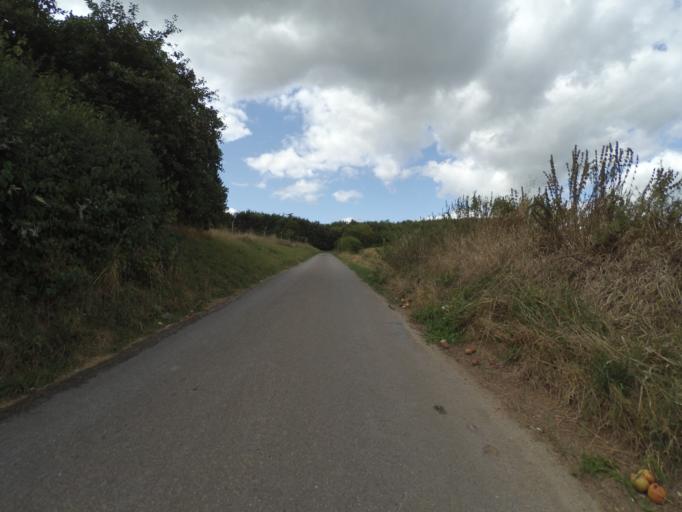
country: LU
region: Grevenmacher
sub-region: Canton de Grevenmacher
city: Betzdorf
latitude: 49.6845
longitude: 6.3403
